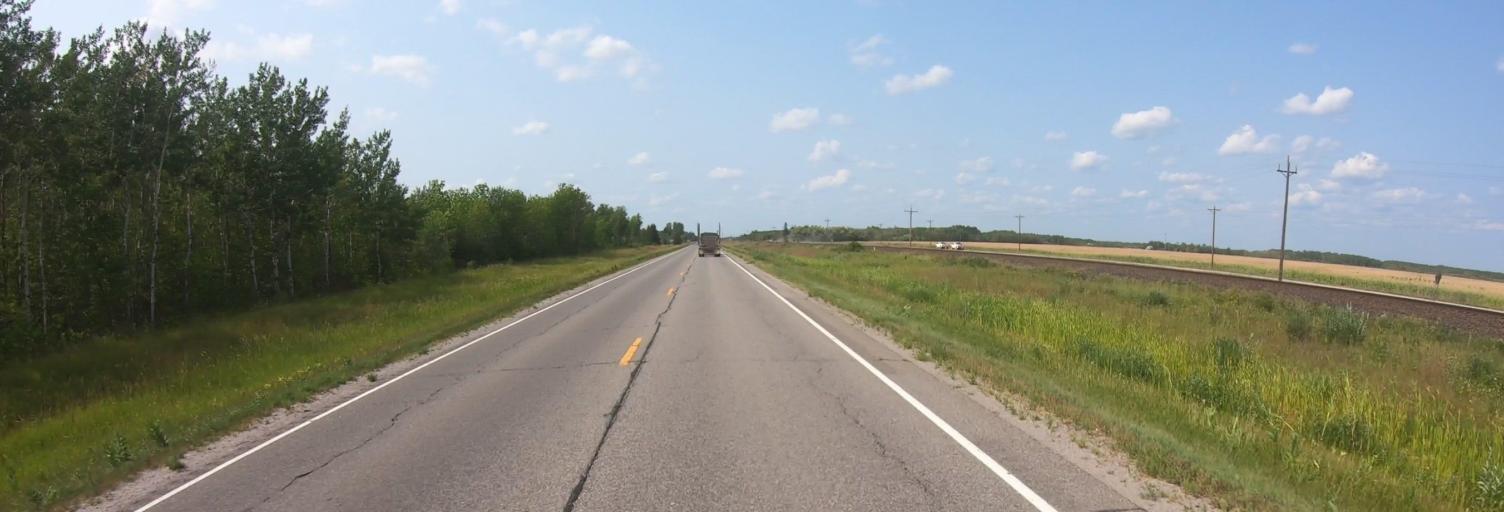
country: US
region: Minnesota
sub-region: Roseau County
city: Warroad
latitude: 48.8814
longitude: -95.2881
